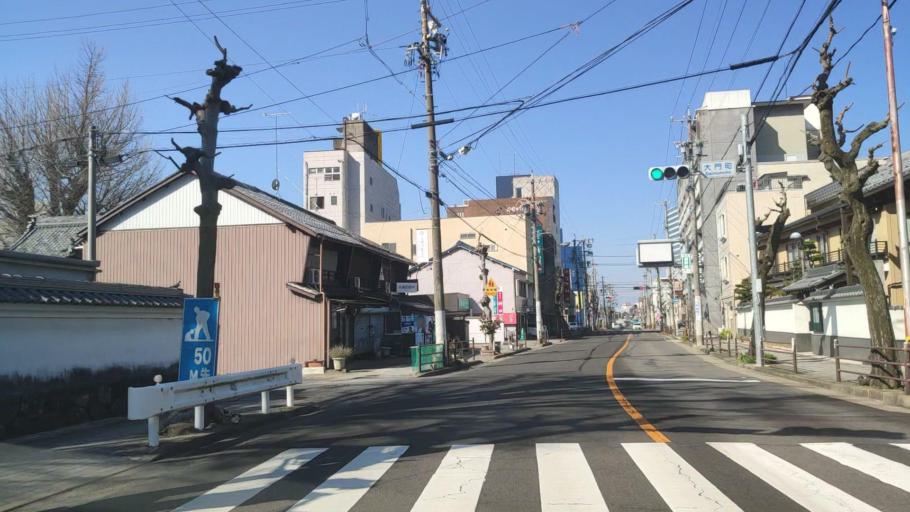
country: JP
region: Gifu
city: Gifu-shi
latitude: 35.4243
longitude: 136.7651
